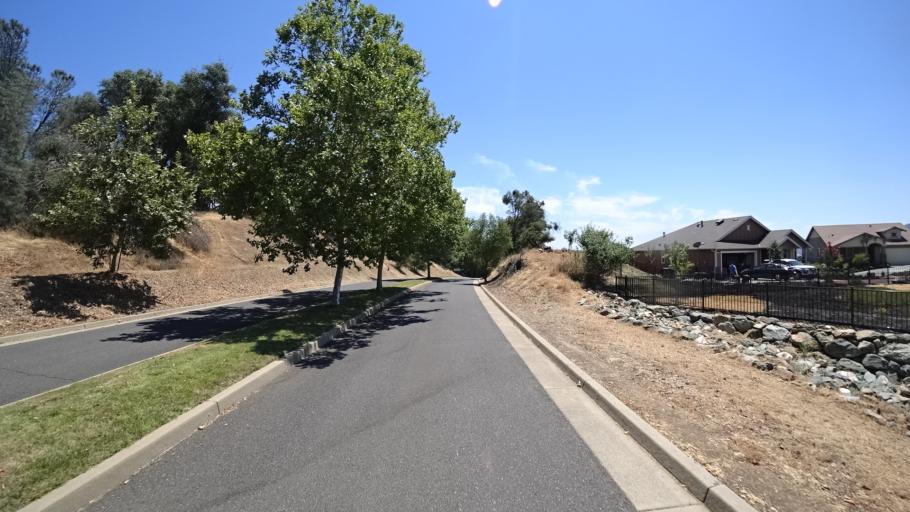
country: US
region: California
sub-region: Calaveras County
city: Angels Camp
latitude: 38.0703
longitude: -120.5525
